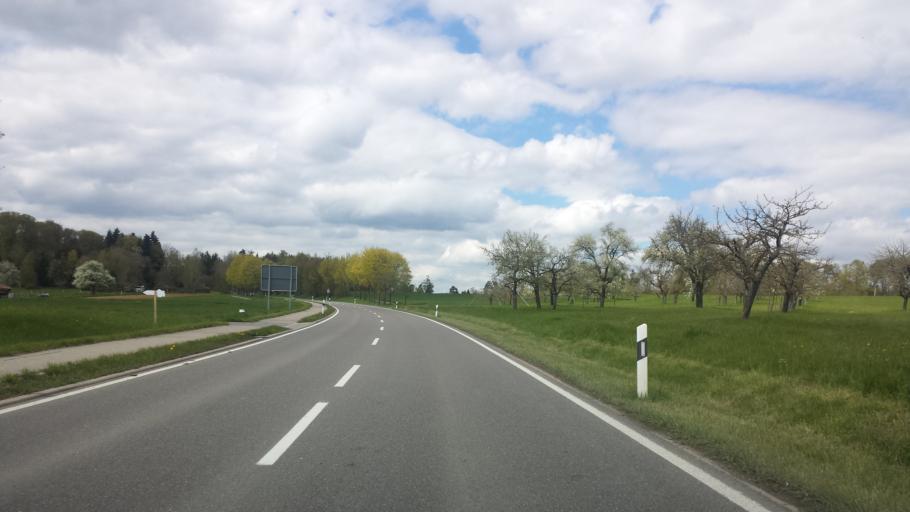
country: DE
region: Baden-Wuerttemberg
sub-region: Regierungsbezirk Stuttgart
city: Rutesheim
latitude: 48.8177
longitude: 8.9377
